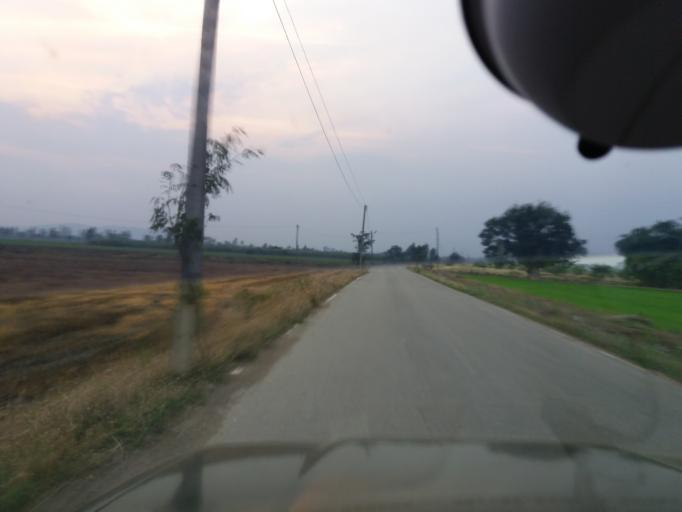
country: TH
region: Suphan Buri
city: Doem Bang Nang Buat
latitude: 14.8868
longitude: 100.1418
